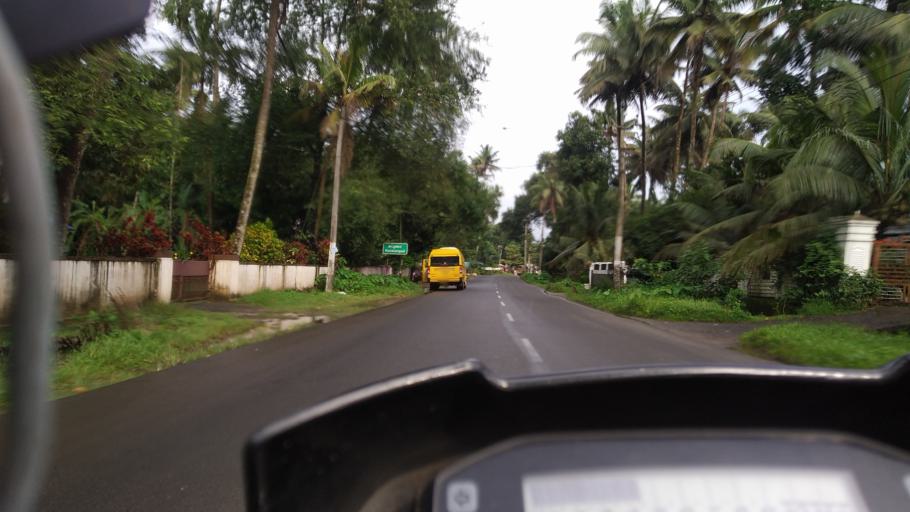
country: IN
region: Kerala
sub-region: Ernakulam
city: Kotamangalam
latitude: 10.0557
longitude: 76.6971
